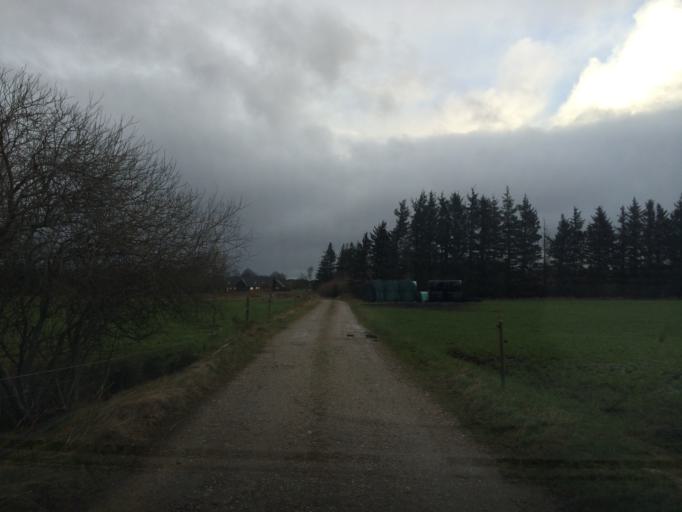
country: DK
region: Central Jutland
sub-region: Holstebro Kommune
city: Ulfborg
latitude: 56.2465
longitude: 8.4168
